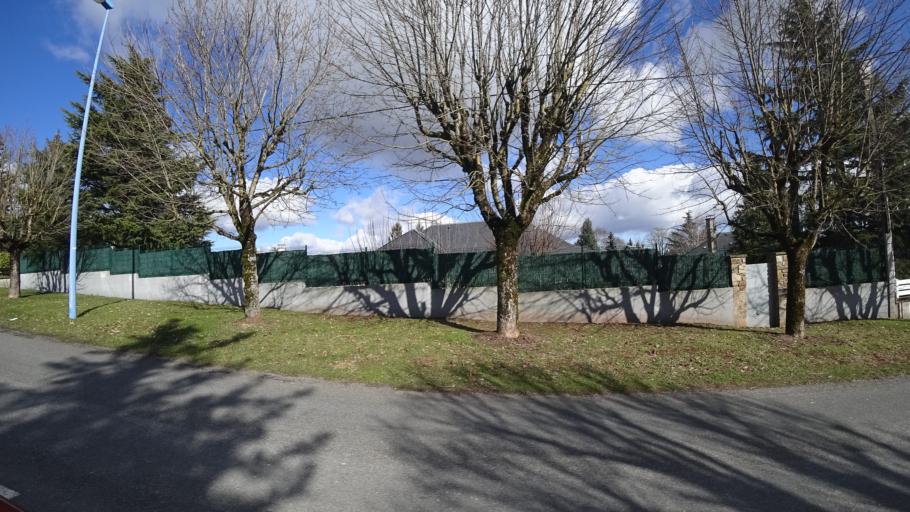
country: FR
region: Midi-Pyrenees
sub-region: Departement de l'Aveyron
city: Olemps
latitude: 44.3723
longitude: 2.5518
